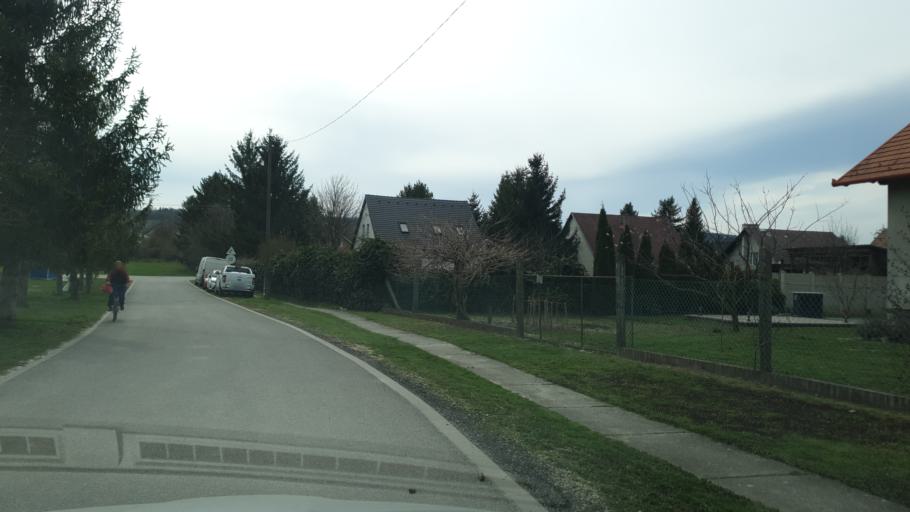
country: HU
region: Fejer
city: Etyek
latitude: 47.4485
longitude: 18.7512
